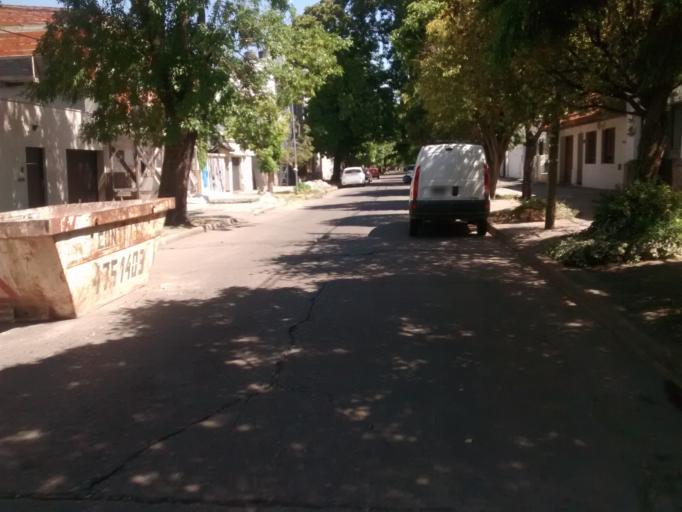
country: AR
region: Buenos Aires
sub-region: Partido de La Plata
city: La Plata
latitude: -34.9293
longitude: -57.9349
